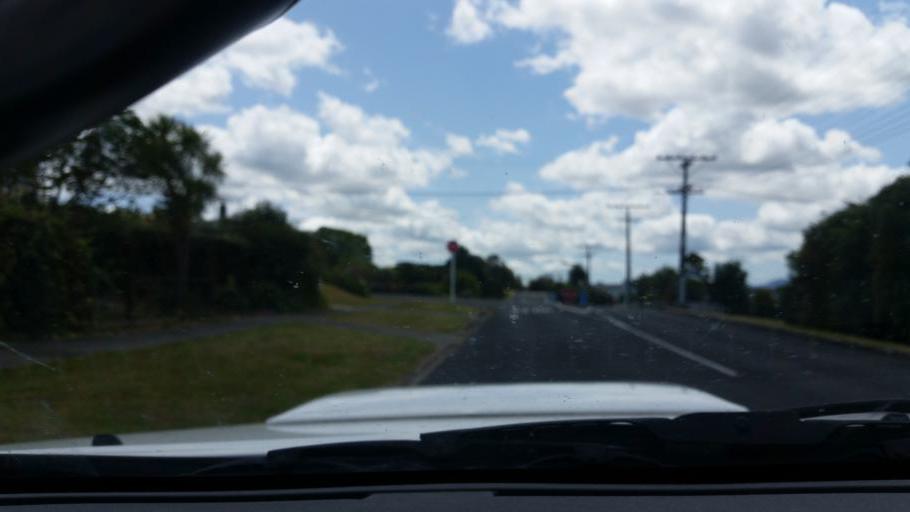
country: NZ
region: Northland
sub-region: Kaipara District
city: Dargaville
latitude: -35.9349
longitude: 173.8686
